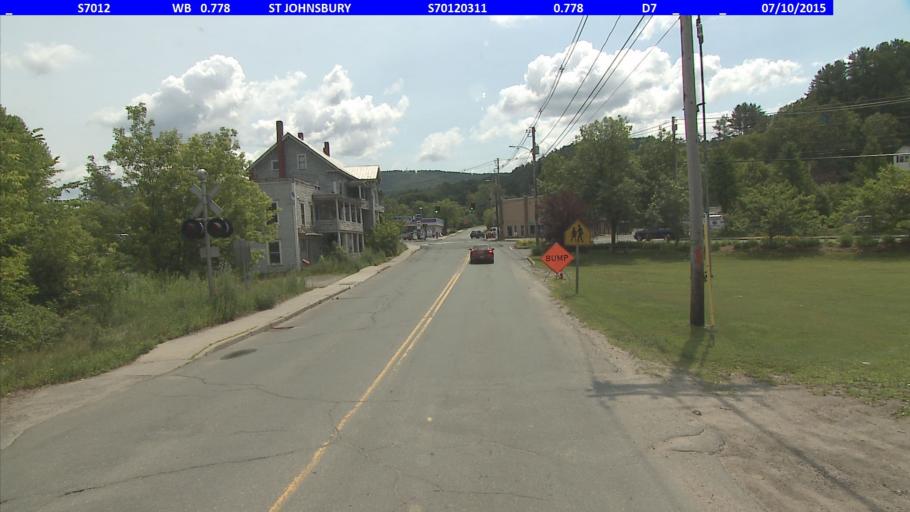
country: US
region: Vermont
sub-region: Caledonia County
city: Saint Johnsbury
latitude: 44.4215
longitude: -72.0051
